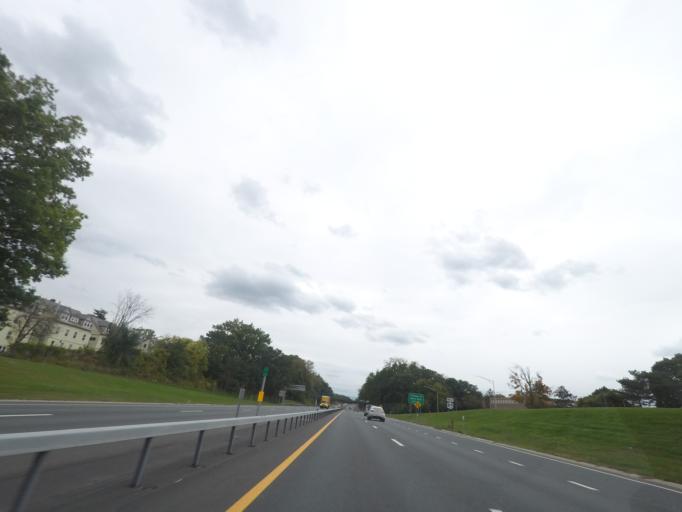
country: US
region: New York
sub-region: Albany County
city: Roessleville
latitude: 42.6735
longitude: -73.8060
